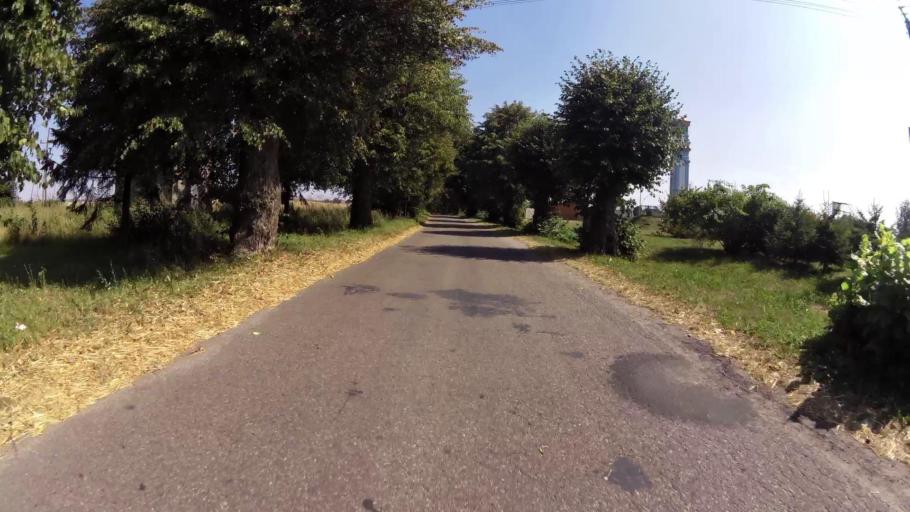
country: PL
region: West Pomeranian Voivodeship
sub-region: Powiat walecki
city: Walcz
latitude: 53.2006
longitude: 16.5006
